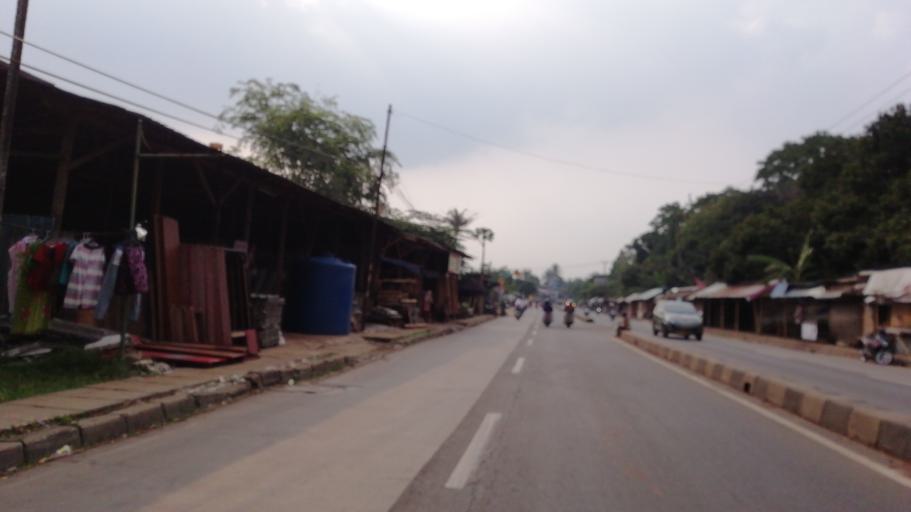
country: ID
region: West Java
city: Parung
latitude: -6.4849
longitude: 106.7353
